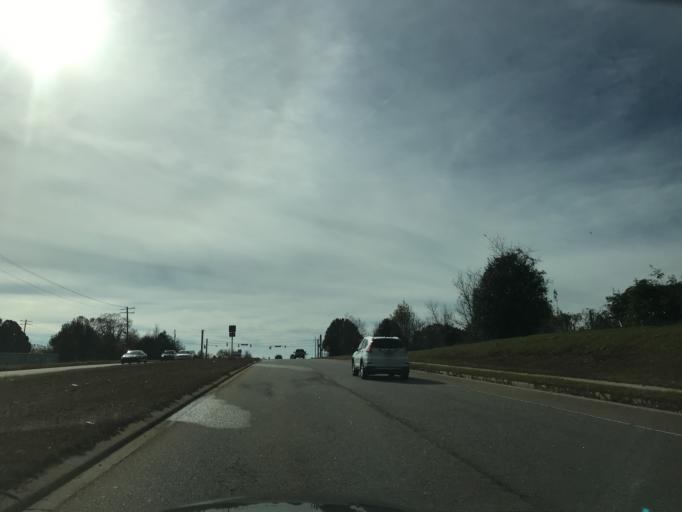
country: US
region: North Carolina
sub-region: Wake County
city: West Raleigh
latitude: 35.8171
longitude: -78.7135
